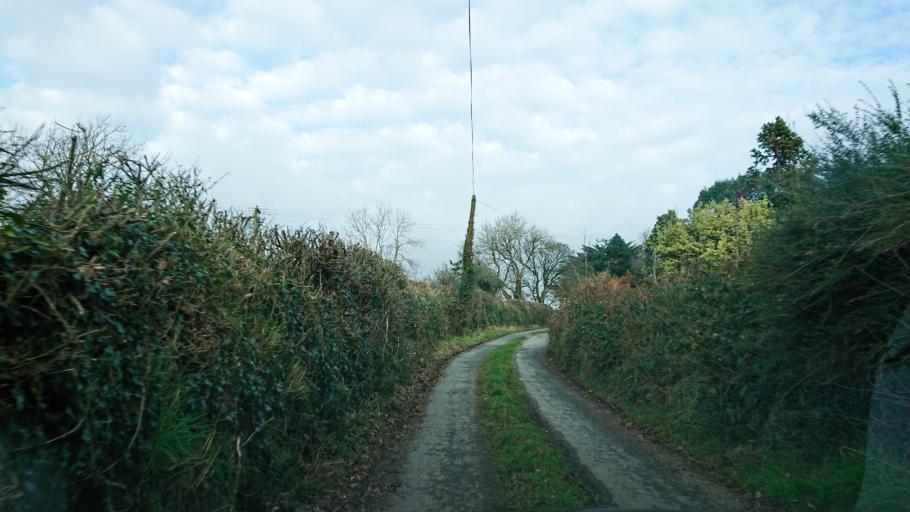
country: IE
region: Munster
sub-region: Waterford
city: Tra Mhor
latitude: 52.1655
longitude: -7.2739
